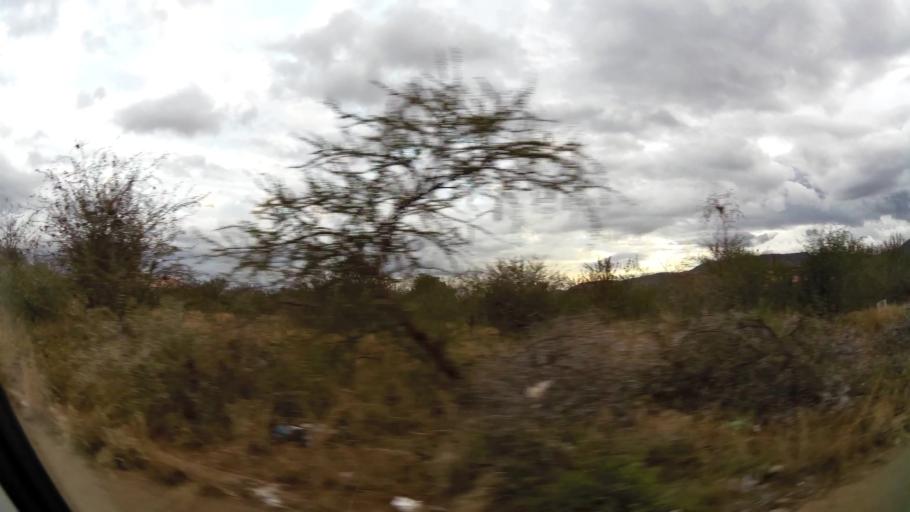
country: ZA
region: Limpopo
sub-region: Waterberg District Municipality
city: Mokopane
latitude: -24.1949
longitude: 28.9977
